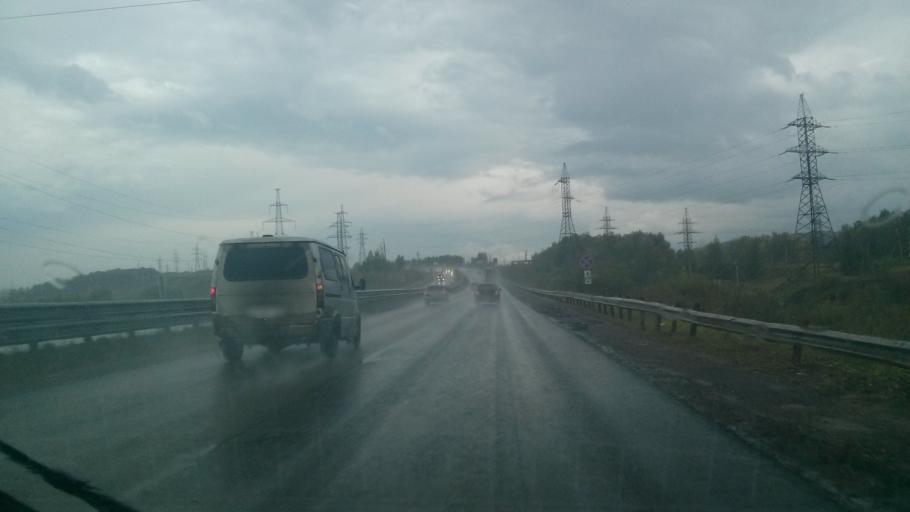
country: RU
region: Nizjnij Novgorod
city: Afonino
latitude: 56.2338
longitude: 44.0573
